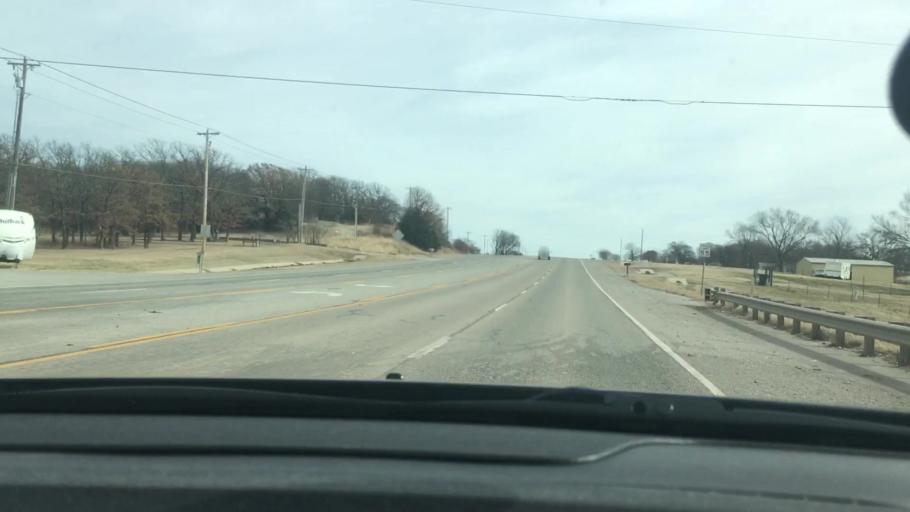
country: US
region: Oklahoma
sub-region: Carter County
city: Dickson
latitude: 34.1871
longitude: -97.0295
